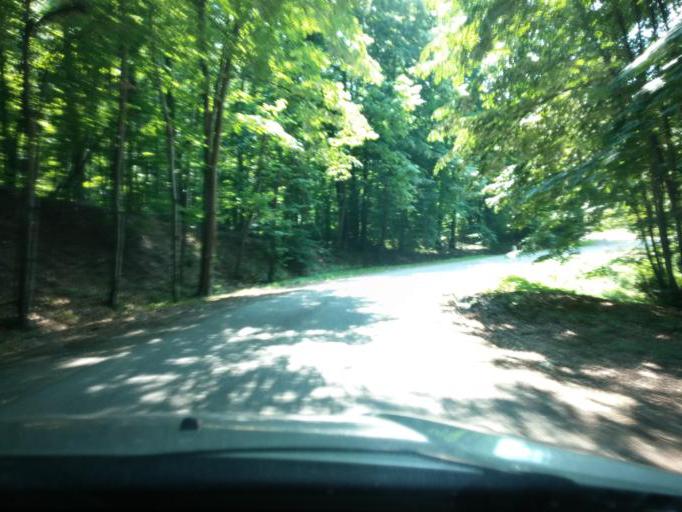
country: HU
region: Somogy
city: Kaposvar
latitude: 46.2549
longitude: 17.8039
